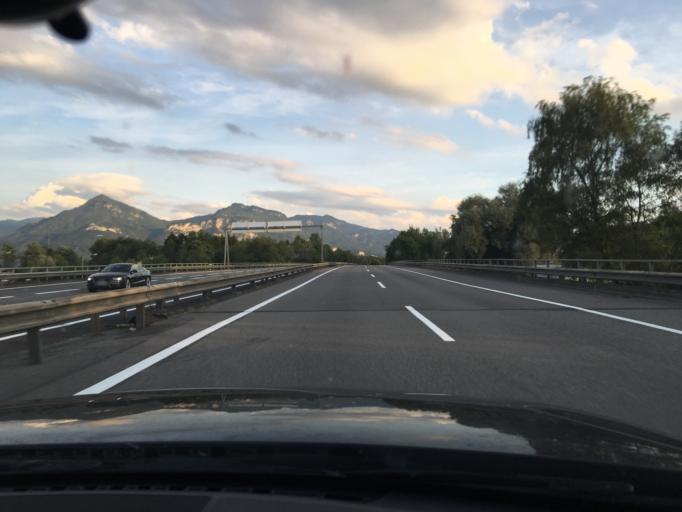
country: AT
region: Vorarlberg
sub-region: Politischer Bezirk Dornbirn
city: Dornbirn
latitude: 47.4420
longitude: 9.7229
